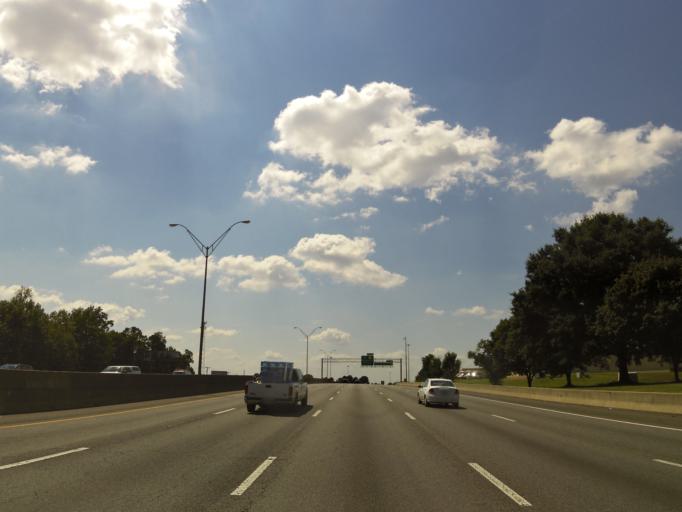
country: US
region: North Carolina
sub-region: Mecklenburg County
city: Charlotte
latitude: 35.2736
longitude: -80.8303
